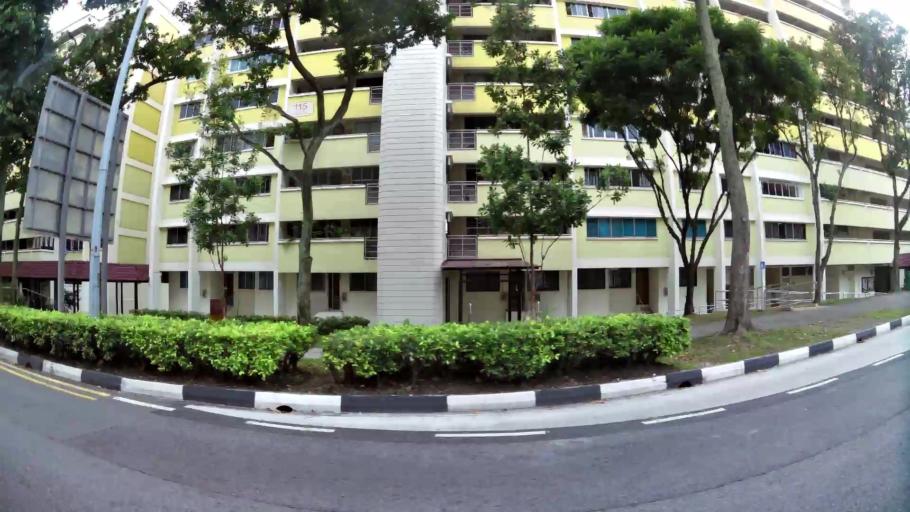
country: SG
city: Singapore
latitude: 1.3482
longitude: 103.8488
